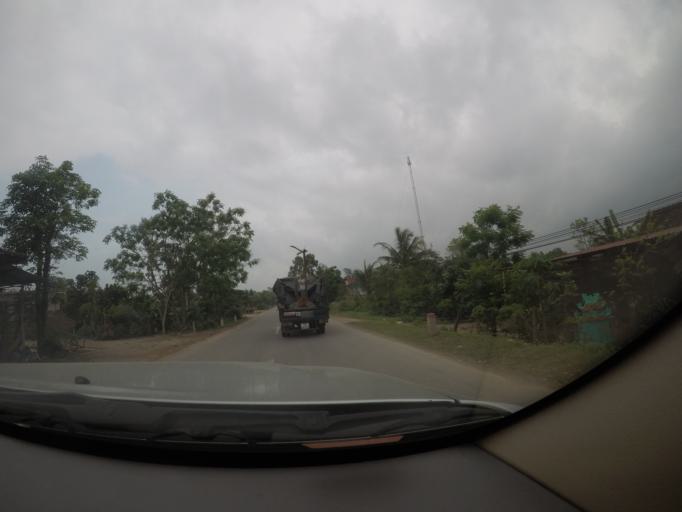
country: VN
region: Quang Binh
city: Kien Giang
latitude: 17.2242
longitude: 106.7047
